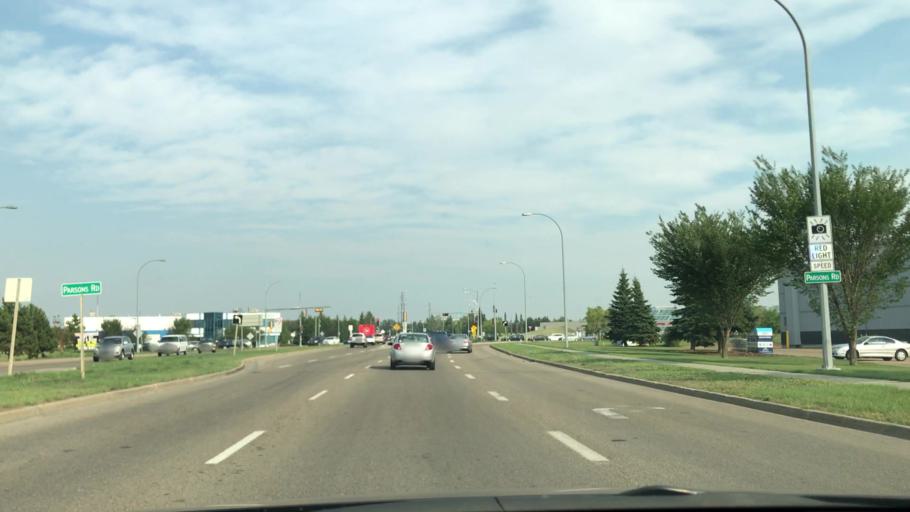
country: CA
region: Alberta
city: Edmonton
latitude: 53.4534
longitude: -113.4816
